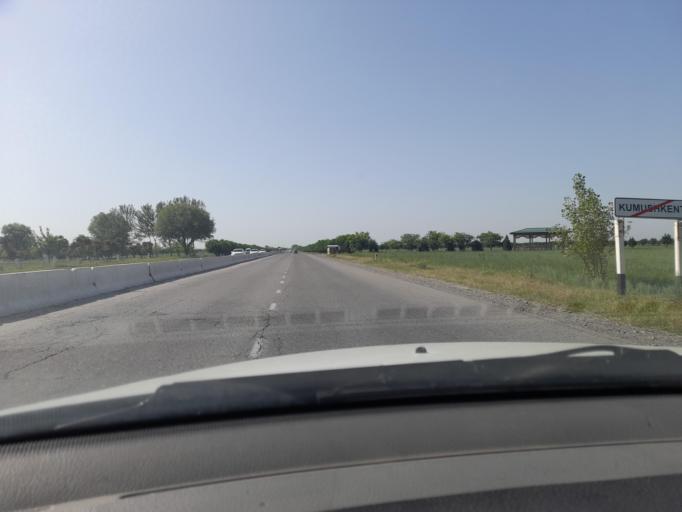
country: UZ
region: Samarqand
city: Daxbet
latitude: 39.8206
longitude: 66.8452
